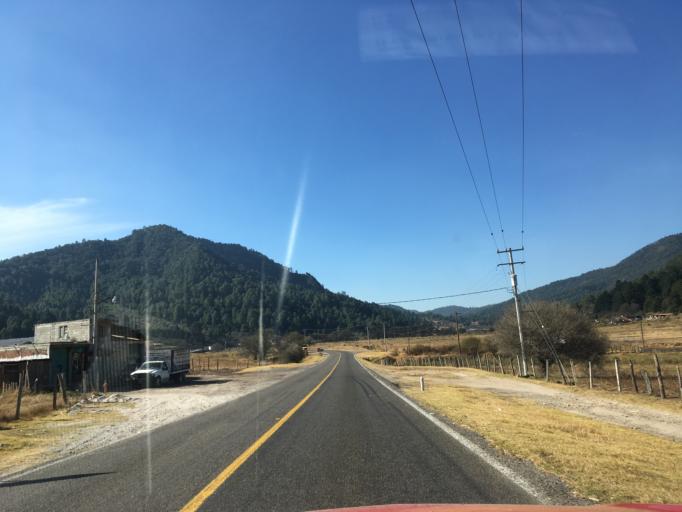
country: MX
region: Michoacan
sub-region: Hidalgo
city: Tierras Coloradas (San Pedro)
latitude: 19.6763
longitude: -100.7376
